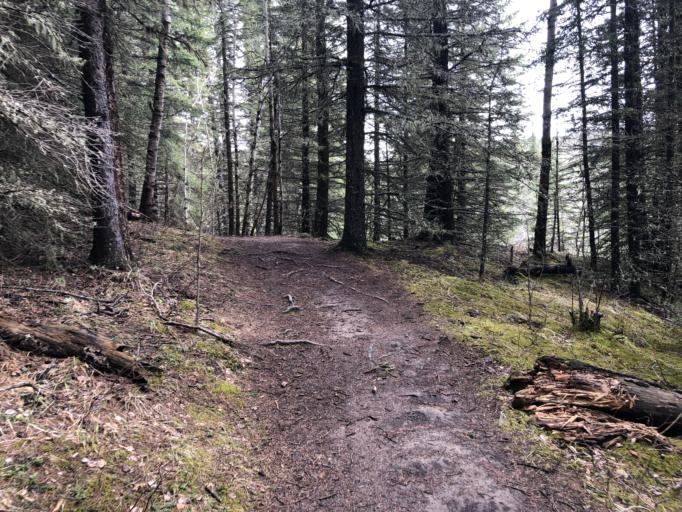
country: CA
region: Alberta
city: Cochrane
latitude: 51.0416
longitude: -114.7573
